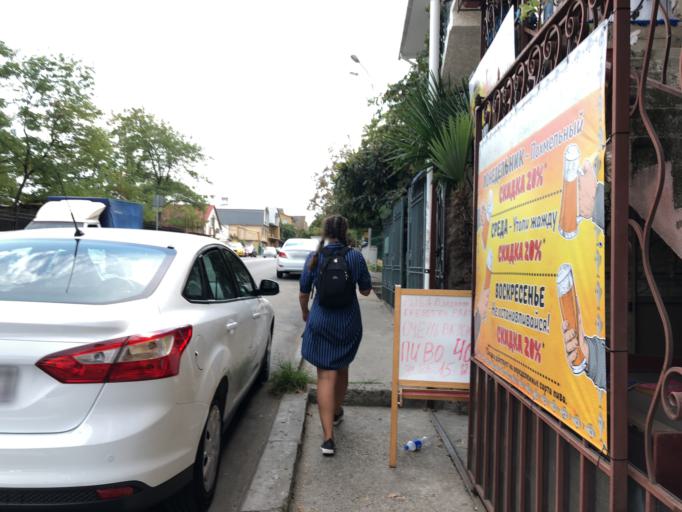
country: RU
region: Krasnodarskiy
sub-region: Sochi City
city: Sochi
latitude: 43.5943
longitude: 39.7418
